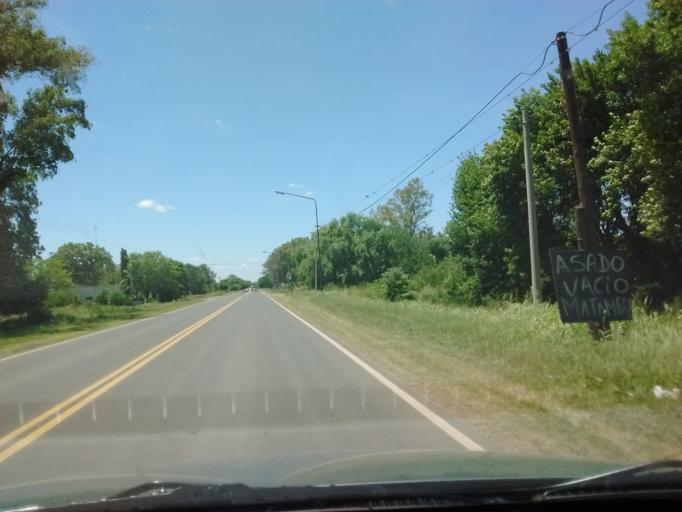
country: AR
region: Entre Rios
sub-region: Departamento de Gualeguay
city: Gualeguay
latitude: -33.1240
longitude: -59.3350
